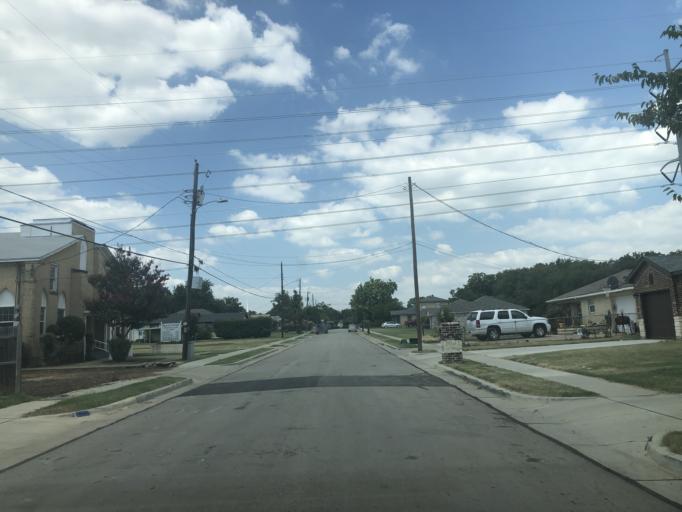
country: US
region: Texas
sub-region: Dallas County
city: Grand Prairie
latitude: 32.7341
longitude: -97.0336
